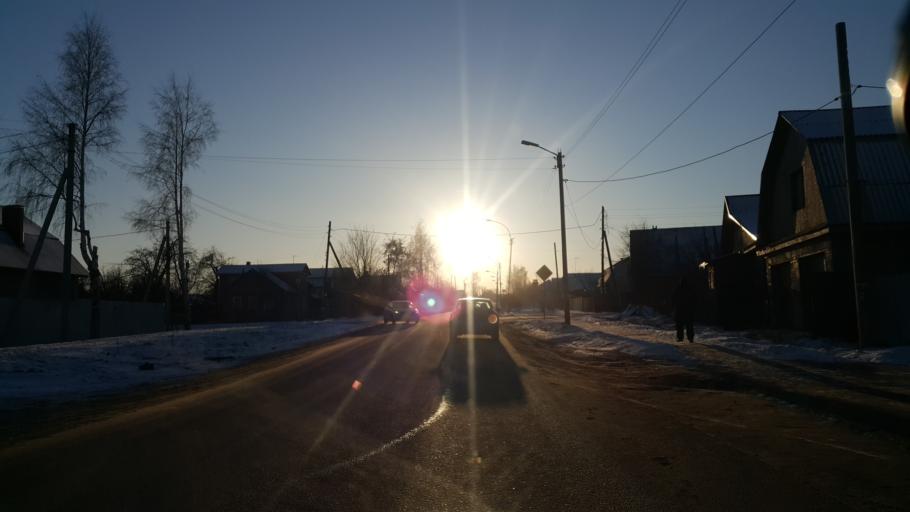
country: RU
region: Tambov
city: Pokrovo-Prigorodnoye
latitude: 52.7032
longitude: 41.4079
